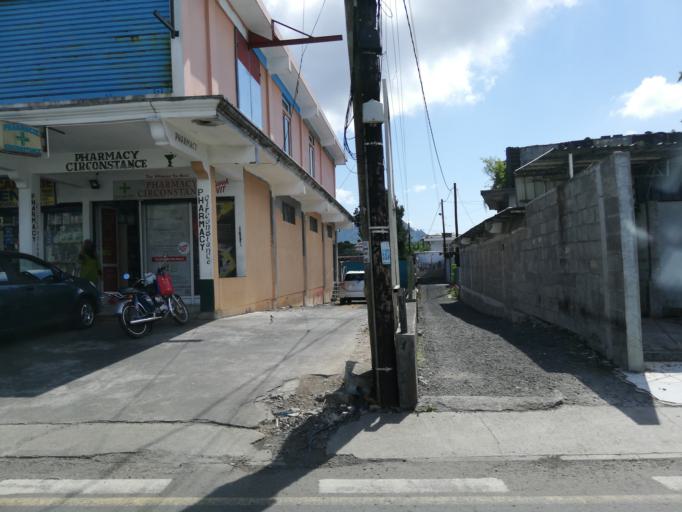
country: MU
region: Moka
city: Verdun
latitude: -20.2230
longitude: 57.5405
